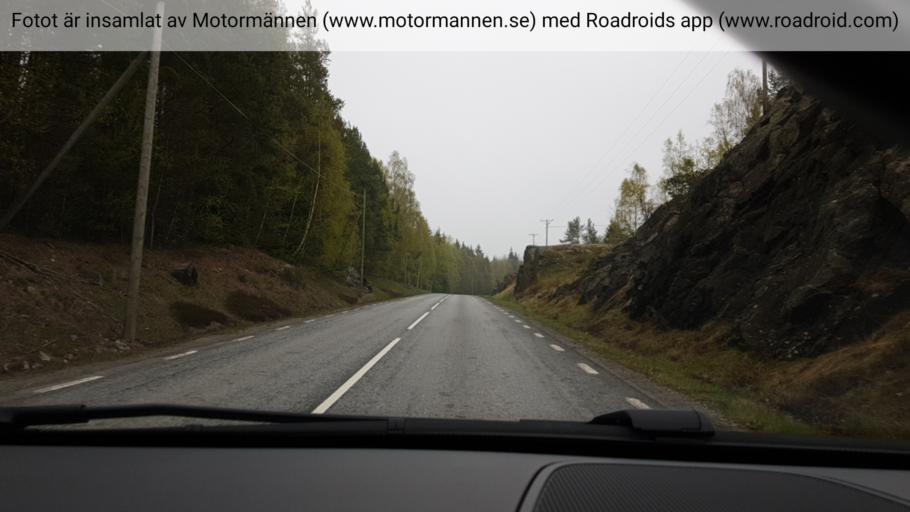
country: SE
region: Stockholm
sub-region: Nynashamns Kommun
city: Nynashamn
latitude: 58.9626
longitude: 17.9930
